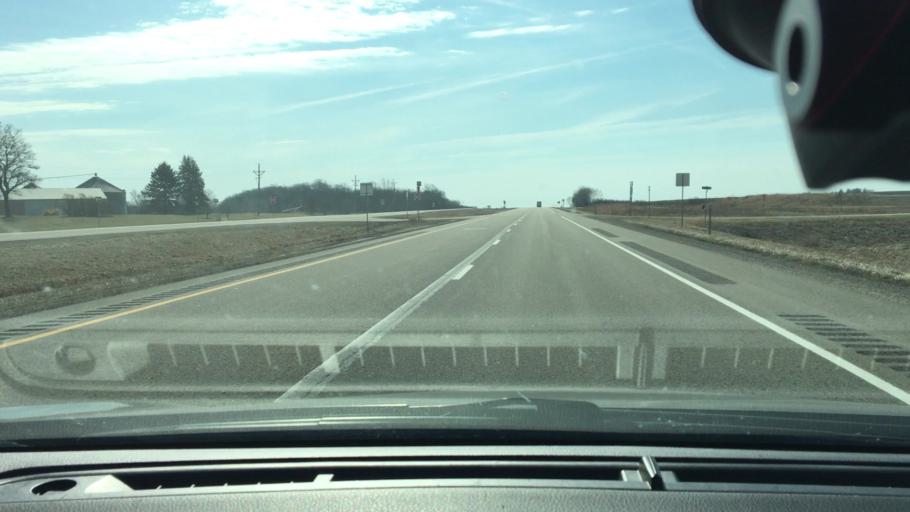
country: US
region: Iowa
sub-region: Floyd County
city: Charles City
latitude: 43.0100
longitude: -92.6278
